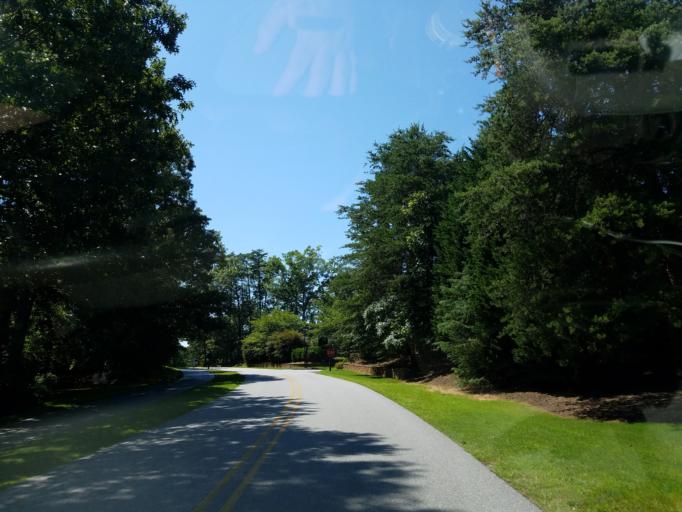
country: US
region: Georgia
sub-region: Lumpkin County
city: Dahlonega
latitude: 34.4057
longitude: -83.9915
